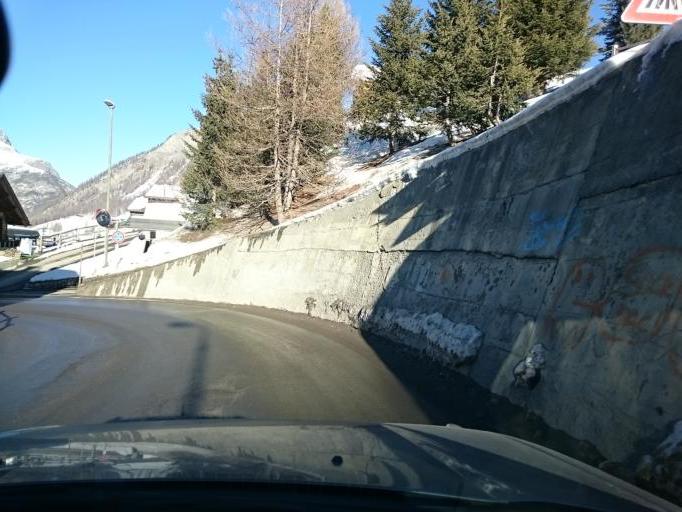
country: IT
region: Lombardy
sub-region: Provincia di Sondrio
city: Livigno
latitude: 46.5368
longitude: 10.1417
